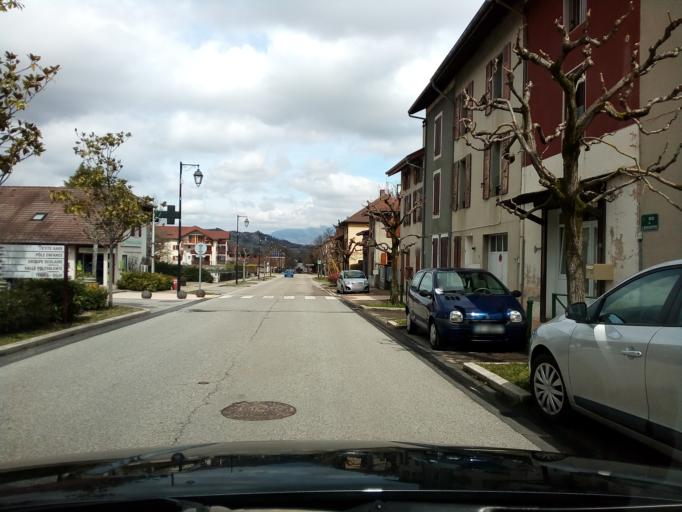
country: FR
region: Rhone-Alpes
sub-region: Departement de l'Isere
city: Chapareillan
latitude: 45.4666
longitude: 5.9899
